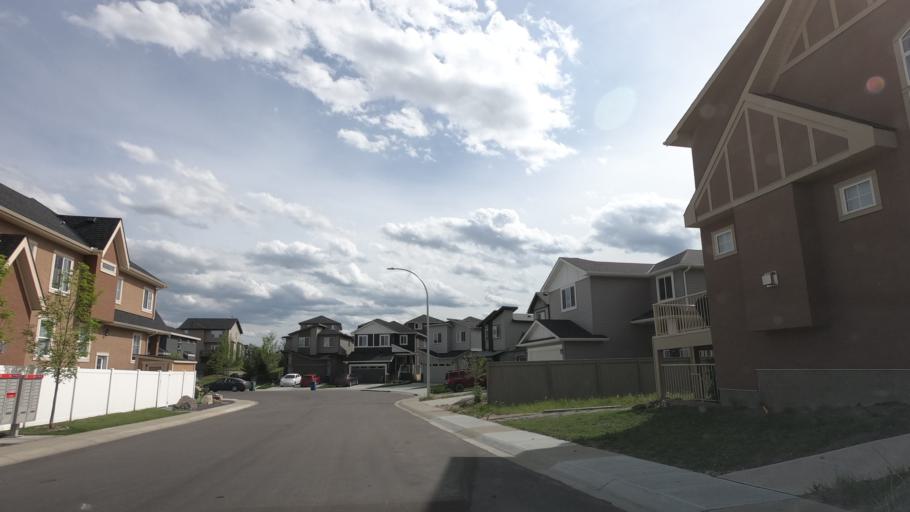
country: CA
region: Alberta
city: Airdrie
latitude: 51.2758
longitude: -114.0464
